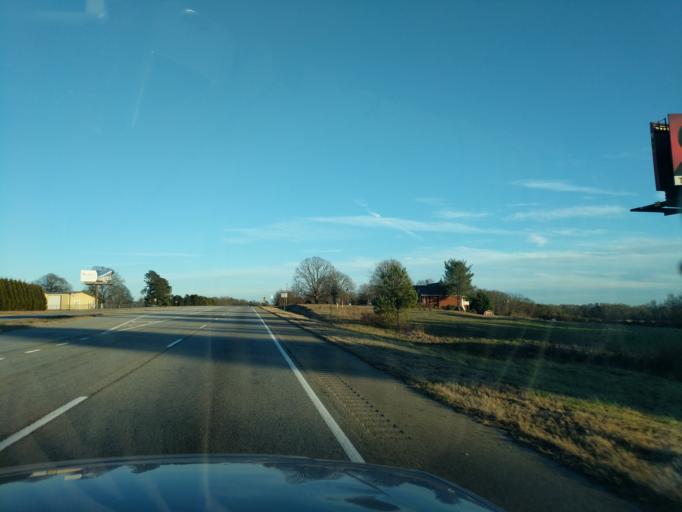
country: US
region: Georgia
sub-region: Franklin County
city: Lavonia
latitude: 34.4547
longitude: -83.1557
